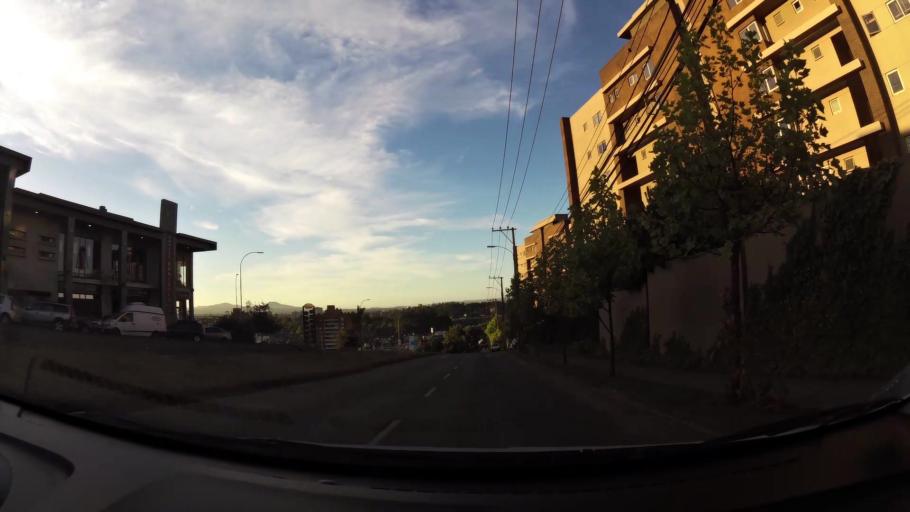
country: CL
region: Biobio
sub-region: Provincia de Concepcion
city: Concepcion
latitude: -36.8469
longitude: -73.0928
